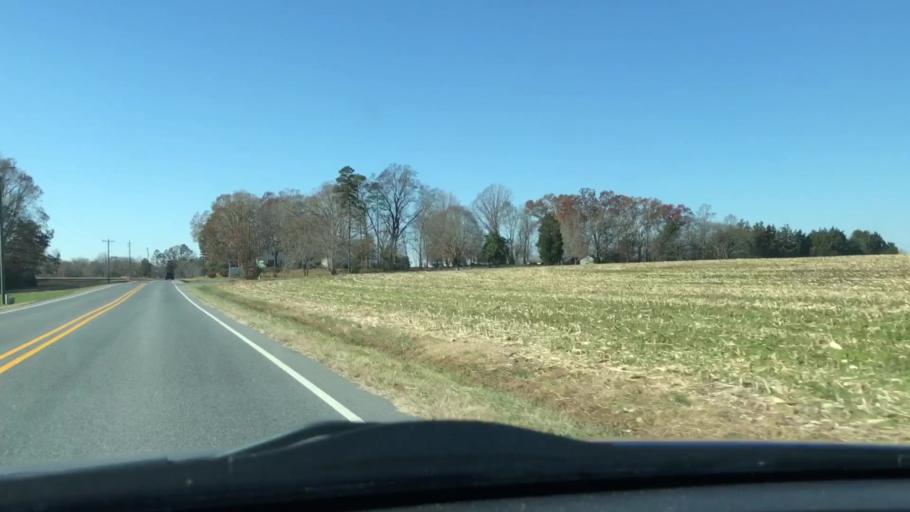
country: US
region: North Carolina
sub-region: Randolph County
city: Asheboro
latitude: 35.6733
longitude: -79.9262
